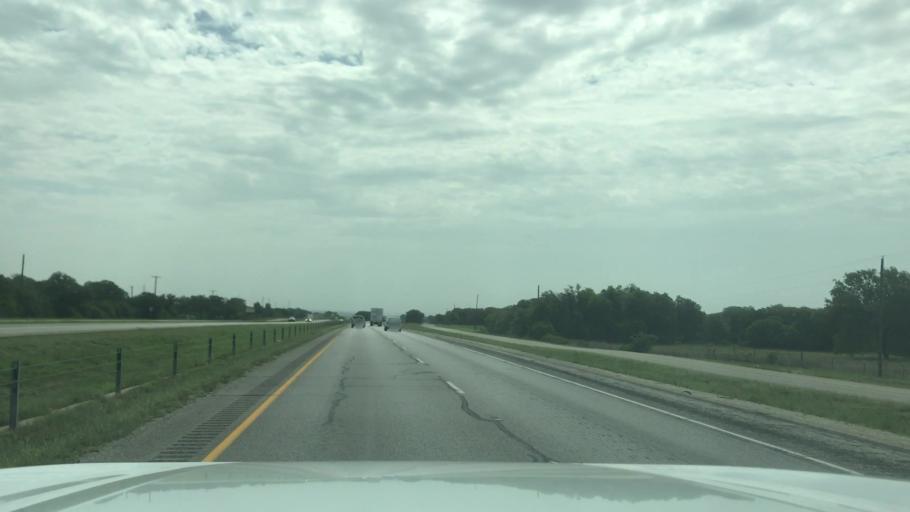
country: US
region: Texas
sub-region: Callahan County
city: Clyde
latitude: 32.4063
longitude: -99.4448
